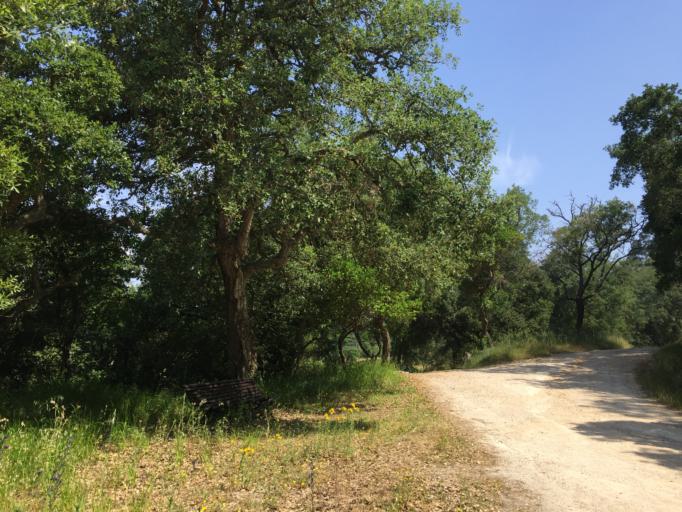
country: PT
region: Lisbon
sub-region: Mafra
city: Milharado
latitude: 38.9052
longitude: -9.1873
